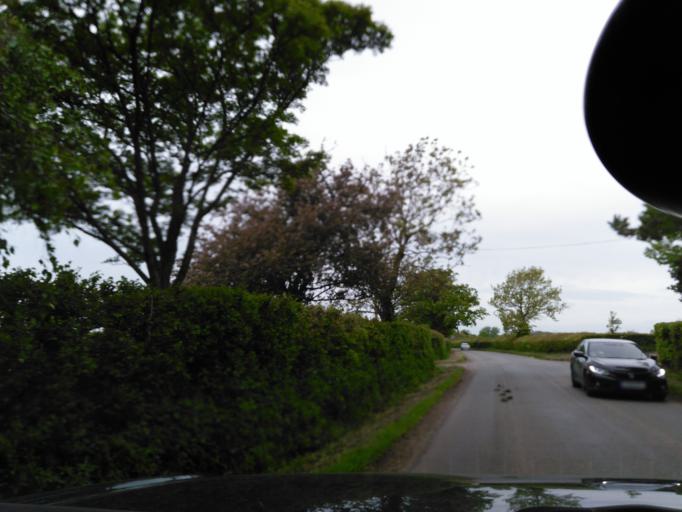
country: GB
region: England
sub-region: Wiltshire
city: Corsham
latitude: 51.4273
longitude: -2.1531
